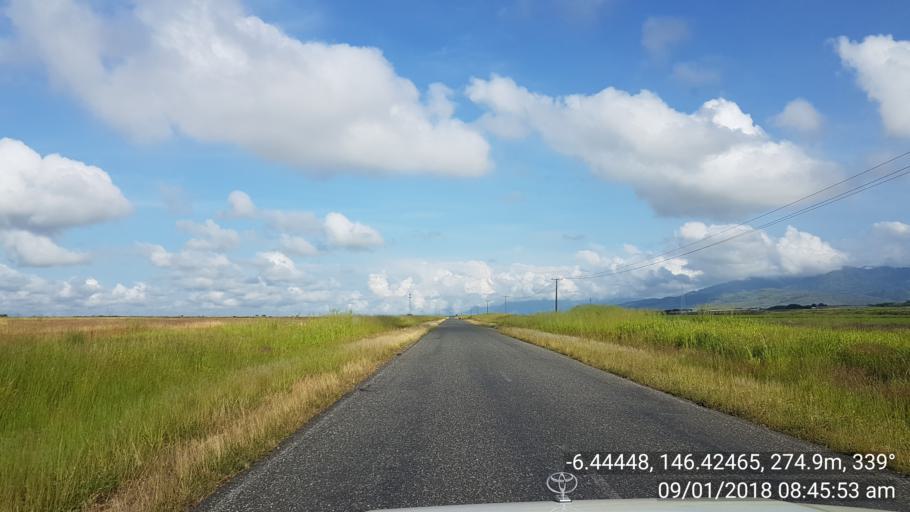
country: PG
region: Eastern Highlands
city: Kainantu
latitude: -6.4435
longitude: 146.4241
